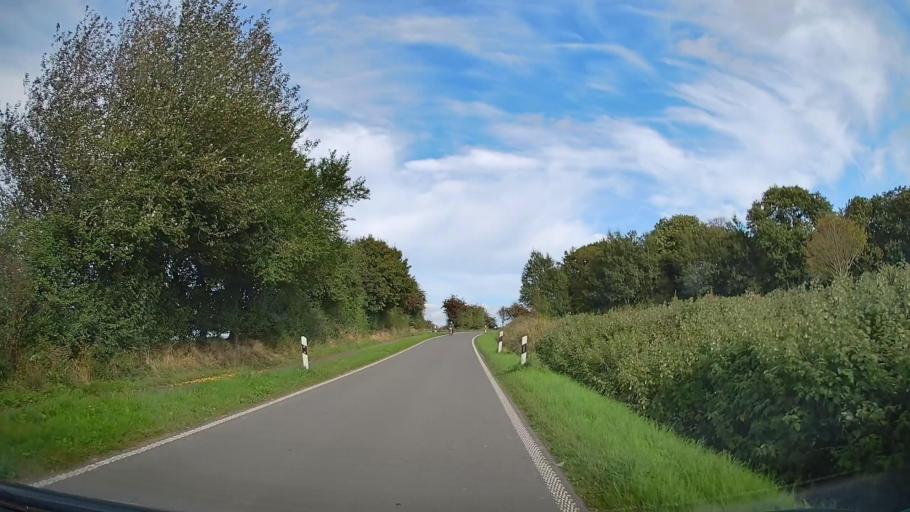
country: DE
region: Schleswig-Holstein
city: Dollerup
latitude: 54.8050
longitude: 9.6984
